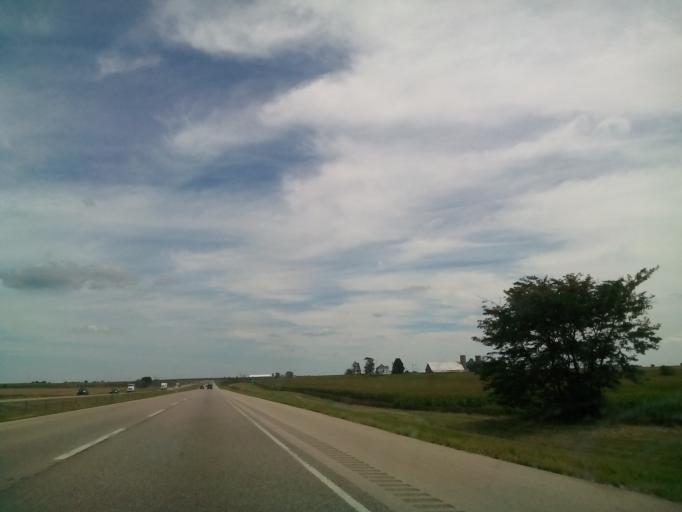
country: US
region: Illinois
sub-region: DeKalb County
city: Malta
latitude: 41.8993
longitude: -88.9337
